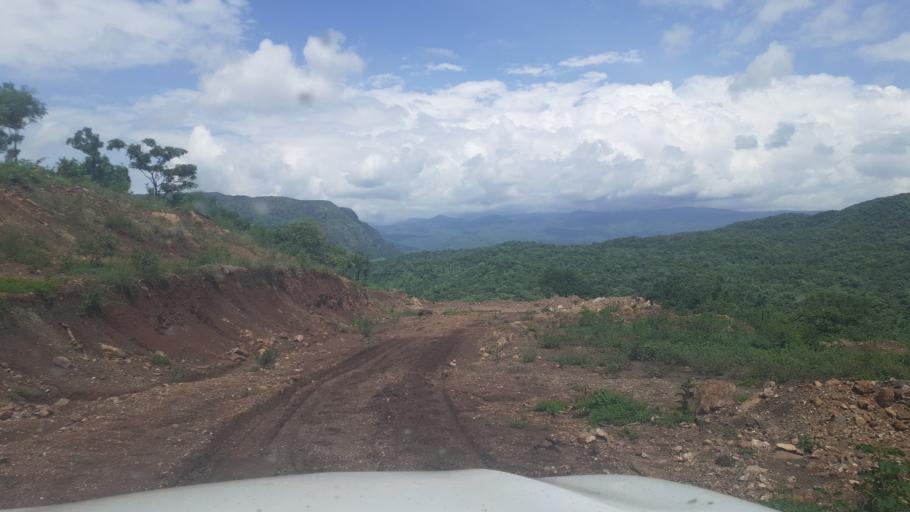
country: ET
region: Southern Nations, Nationalities, and People's Region
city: Areka
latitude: 7.6159
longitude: 37.5149
